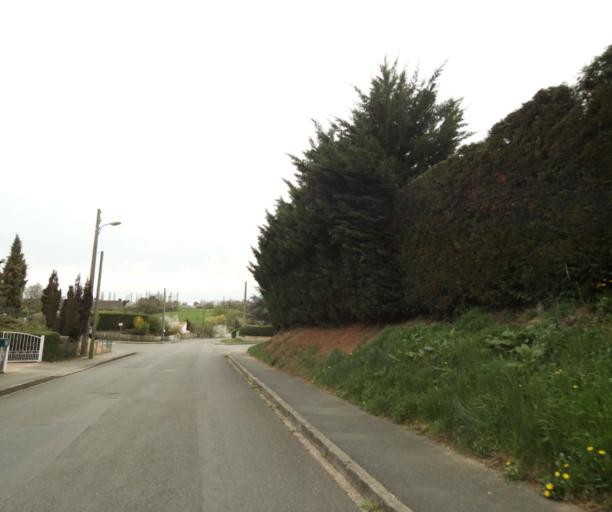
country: FR
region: Bourgogne
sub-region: Departement de Saone-et-Loire
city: Charnay-les-Macon
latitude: 46.3051
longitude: 4.8085
